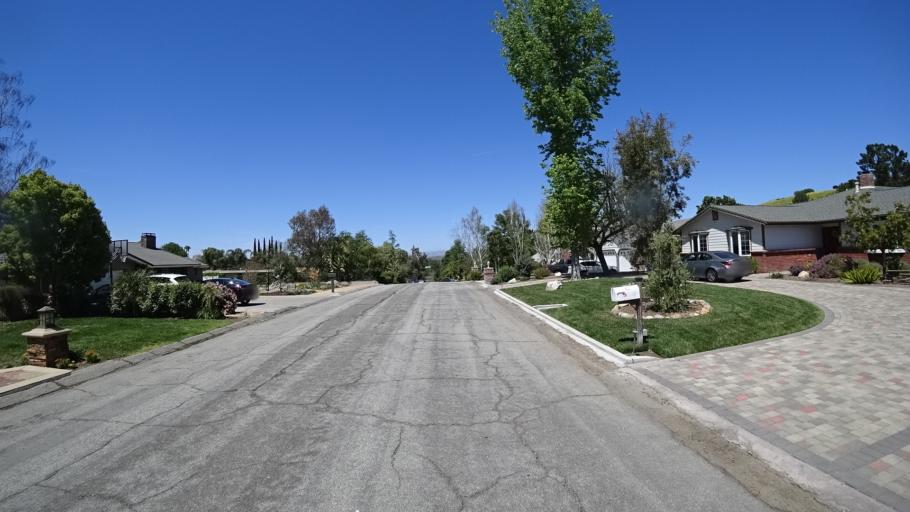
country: US
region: California
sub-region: Ventura County
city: Thousand Oaks
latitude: 34.1948
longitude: -118.8474
